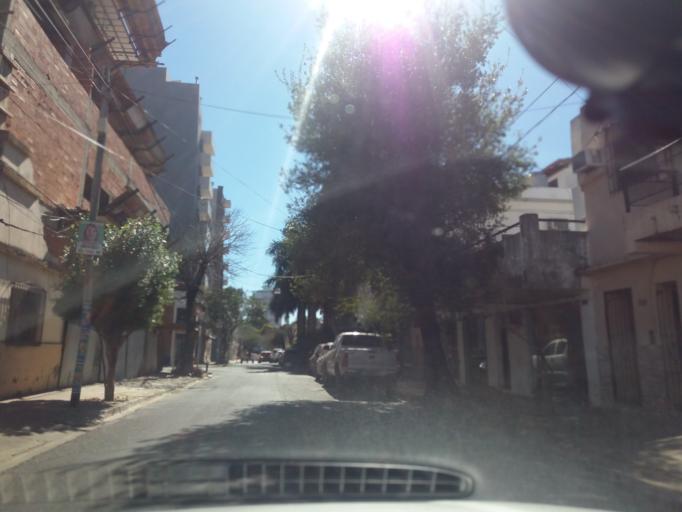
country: AR
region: Corrientes
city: Corrientes
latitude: -27.4674
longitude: -58.8429
